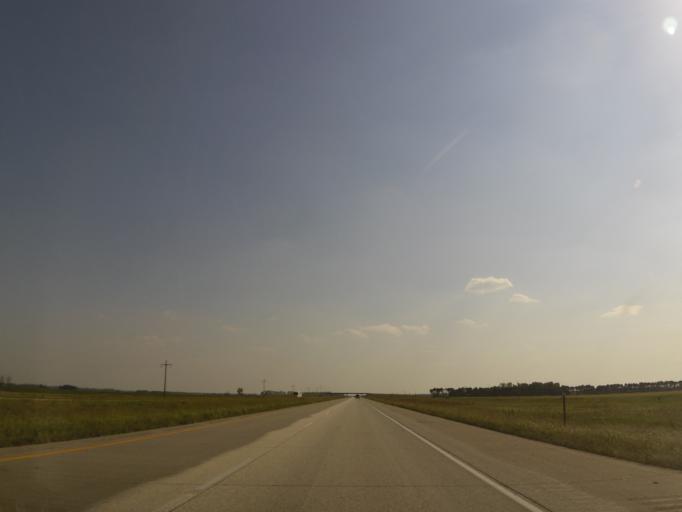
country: US
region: North Dakota
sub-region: Walsh County
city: Grafton
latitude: 48.3329
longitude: -97.1897
